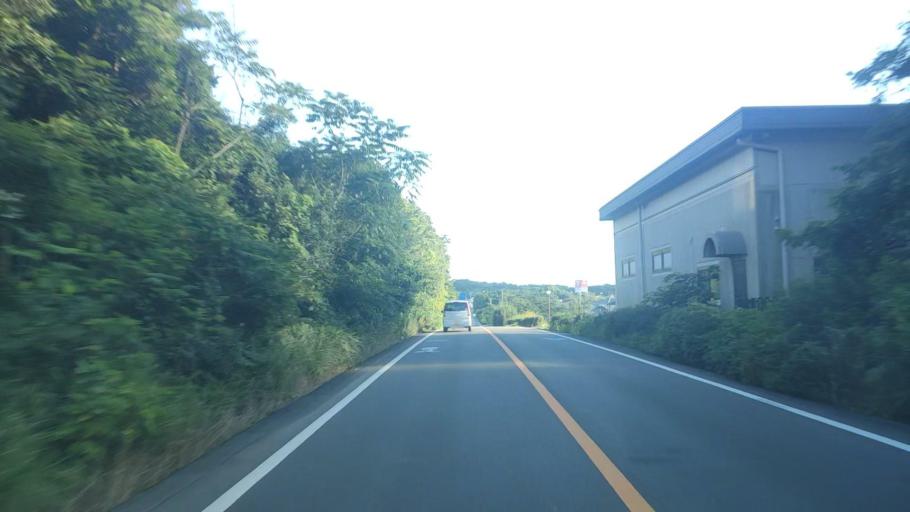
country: JP
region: Mie
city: Toba
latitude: 34.3338
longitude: 136.8407
